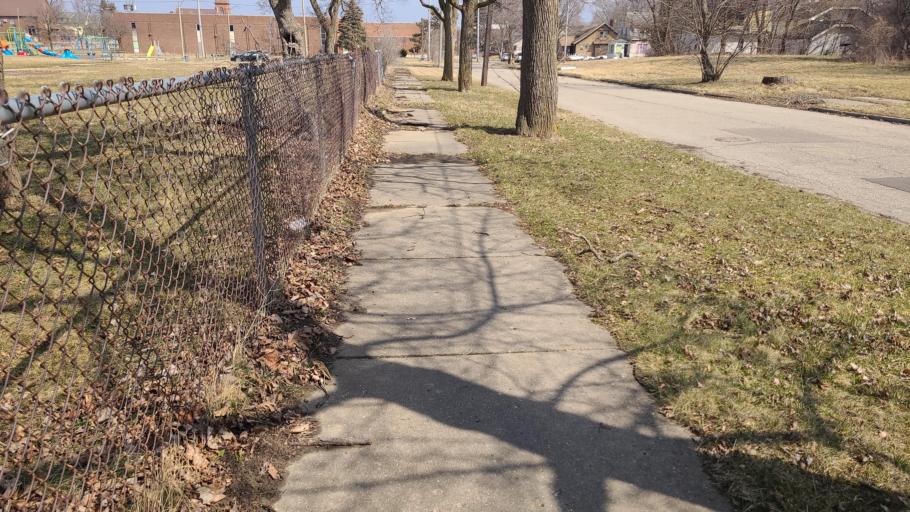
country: US
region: Michigan
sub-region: Genesee County
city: Flint
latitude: 43.0350
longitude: -83.6987
